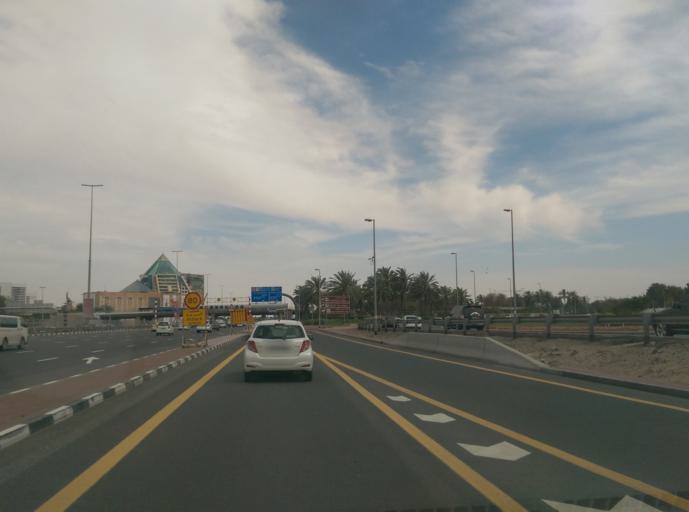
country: AE
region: Ash Shariqah
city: Sharjah
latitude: 25.2307
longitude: 55.3123
